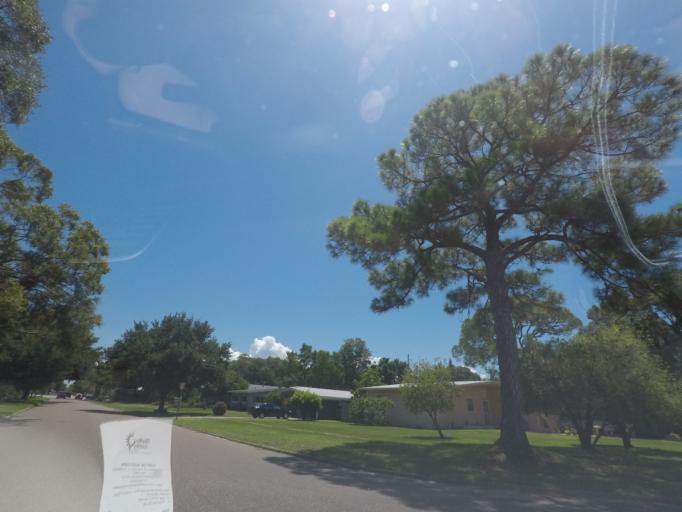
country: US
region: Florida
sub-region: Pinellas County
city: Lealman
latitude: 27.8028
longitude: -82.6405
